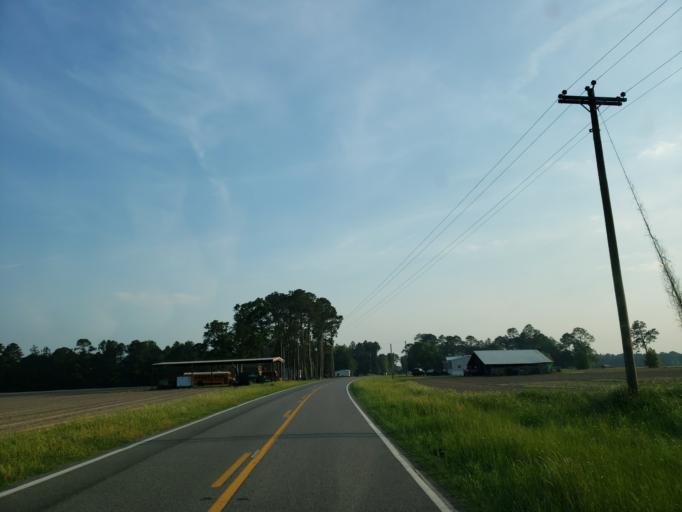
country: US
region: Georgia
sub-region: Cook County
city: Sparks
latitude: 31.2035
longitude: -83.4228
